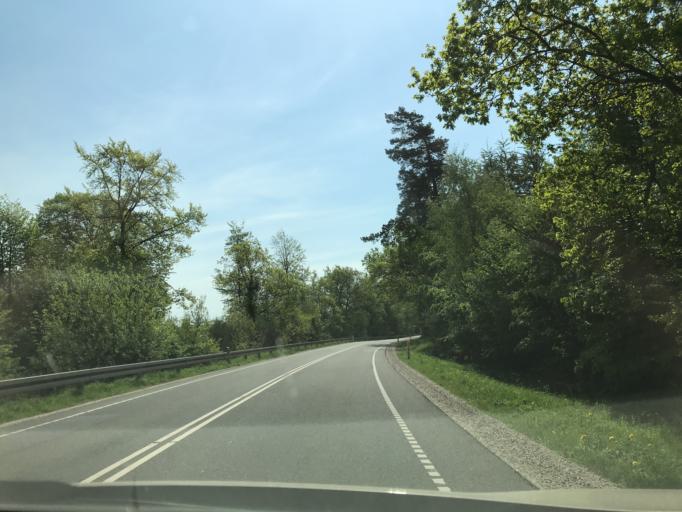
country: DK
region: South Denmark
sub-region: Middelfart Kommune
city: Ejby
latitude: 55.4000
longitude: 9.9009
